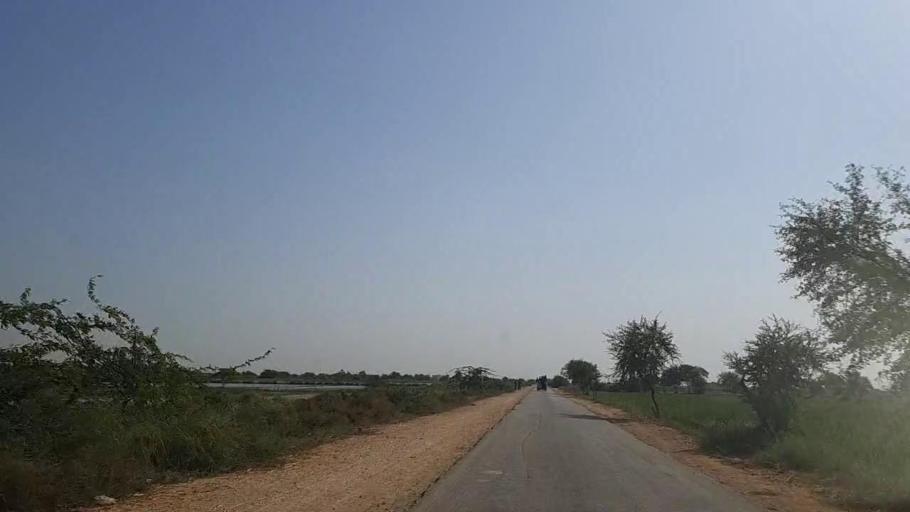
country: PK
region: Sindh
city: Mirpur Batoro
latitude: 24.6531
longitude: 68.2879
